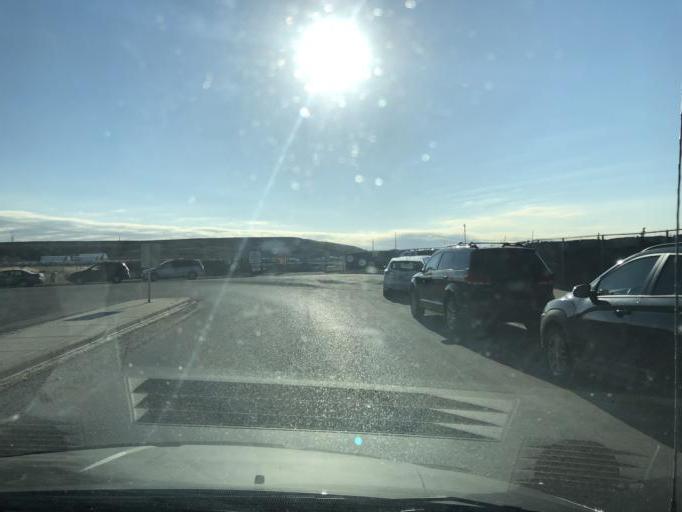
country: CA
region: Alberta
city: Calgary
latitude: 50.9594
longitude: -114.0080
